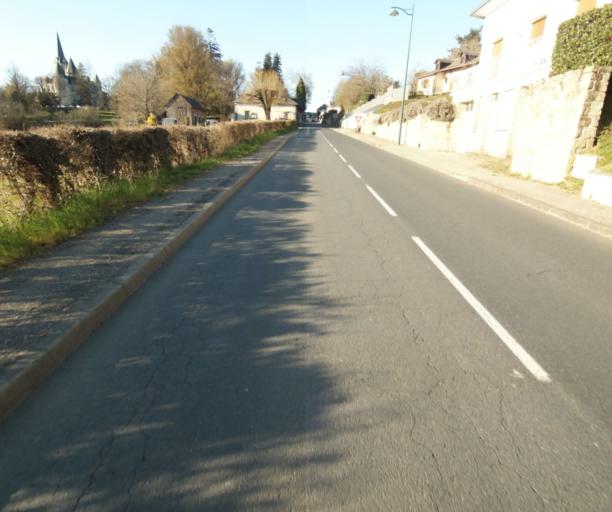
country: FR
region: Limousin
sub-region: Departement de la Correze
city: Seilhac
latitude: 45.3641
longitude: 1.7129
